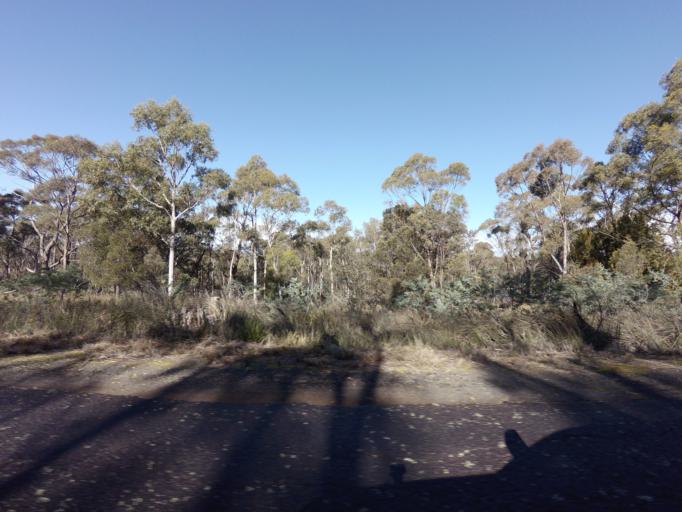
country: AU
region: Tasmania
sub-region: Sorell
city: Sorell
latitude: -42.3617
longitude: 147.9546
